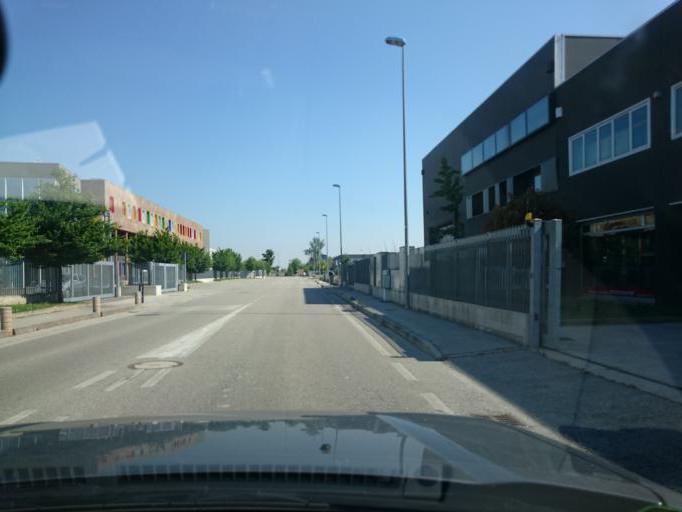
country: IT
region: Veneto
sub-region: Provincia di Padova
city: Oltre Brenta
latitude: 45.4018
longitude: 11.9940
